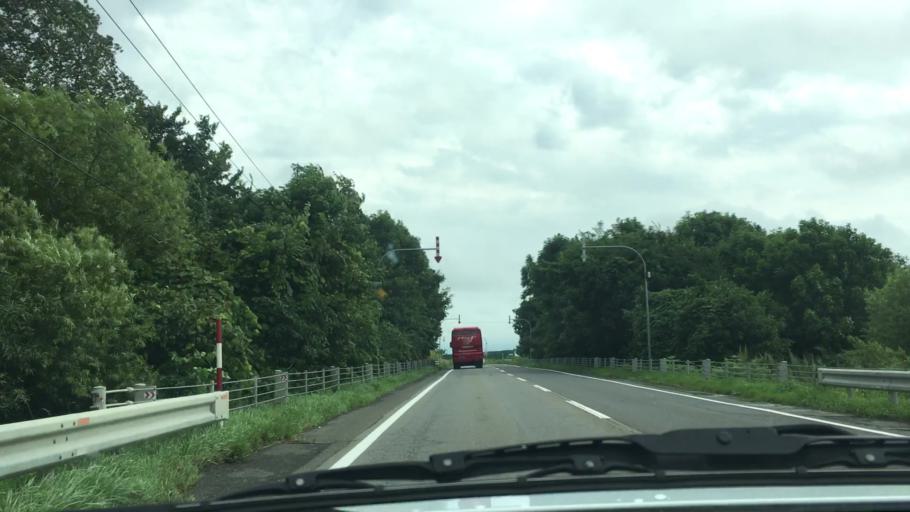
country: JP
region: Hokkaido
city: Chitose
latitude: 42.9428
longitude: 141.7573
